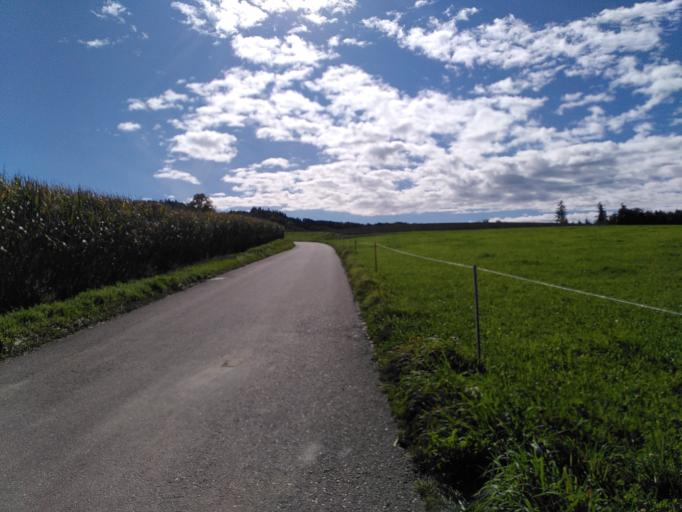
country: CH
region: Bern
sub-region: Oberaargau
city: Seeberg
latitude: 47.1368
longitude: 7.7152
